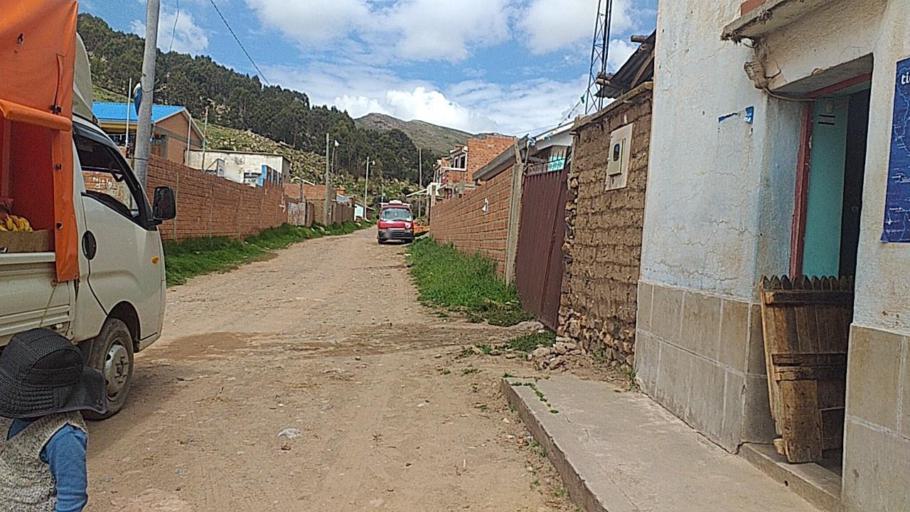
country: BO
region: La Paz
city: Batallas
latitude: -16.3483
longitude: -68.6359
